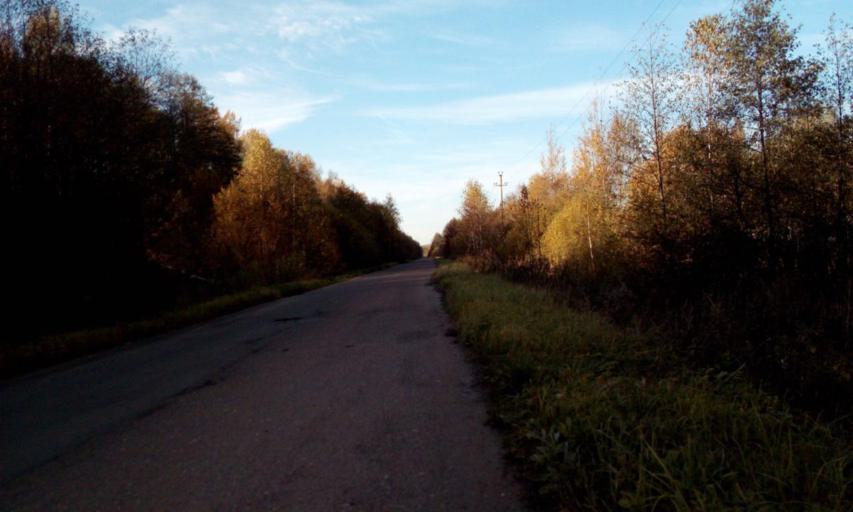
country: RU
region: Moskovskaya
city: Kievskij
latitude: 55.3809
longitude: 36.9098
